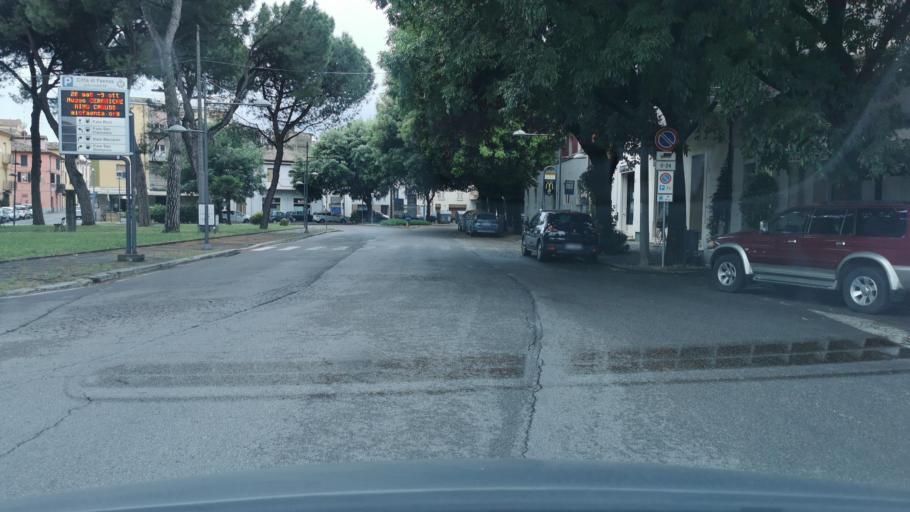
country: IT
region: Emilia-Romagna
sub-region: Provincia di Ravenna
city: Faenza
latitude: 44.2907
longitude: 11.8850
